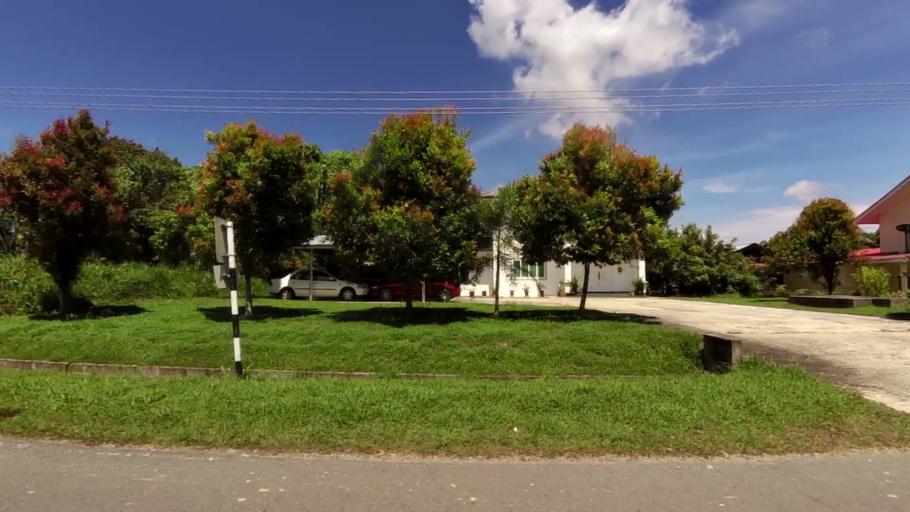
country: BN
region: Brunei and Muara
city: Bandar Seri Begawan
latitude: 4.9367
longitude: 114.9504
